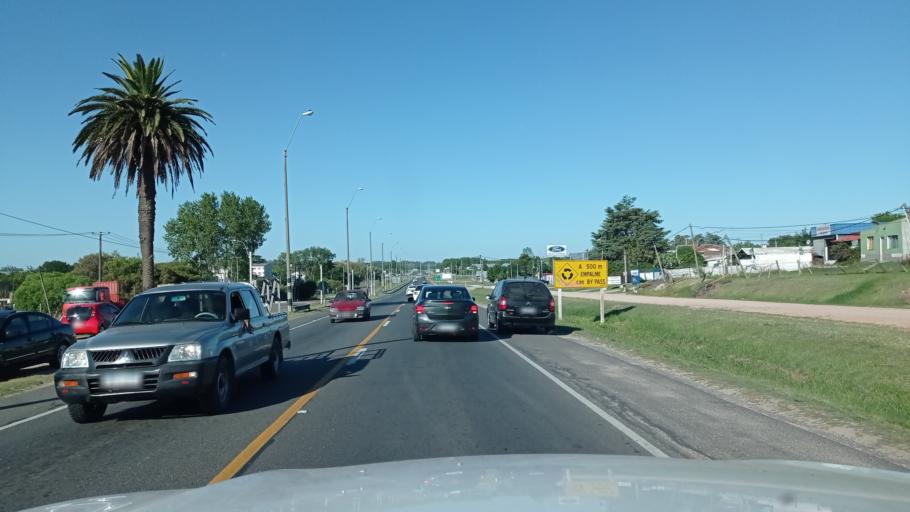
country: UY
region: Canelones
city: Pando
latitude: -34.7209
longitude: -55.9544
